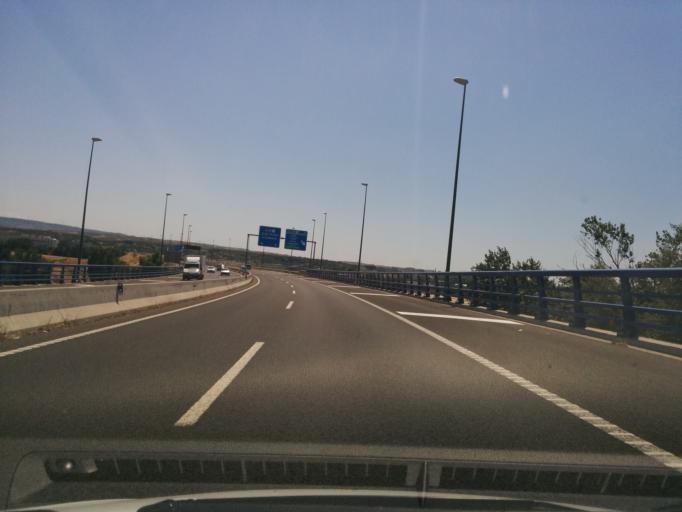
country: ES
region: Aragon
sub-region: Provincia de Zaragoza
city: Zaragoza
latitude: 41.6314
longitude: -0.8403
